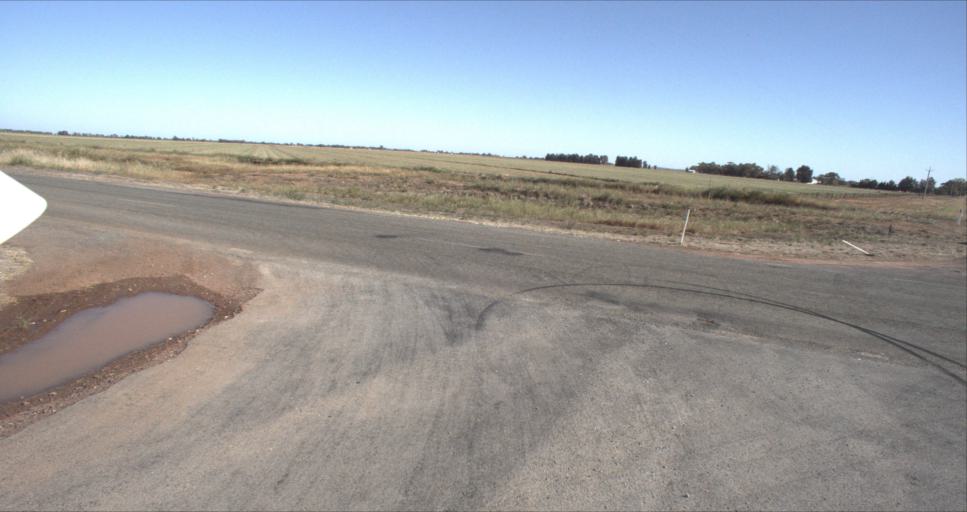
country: AU
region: New South Wales
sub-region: Leeton
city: Leeton
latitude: -34.5502
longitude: 146.3147
